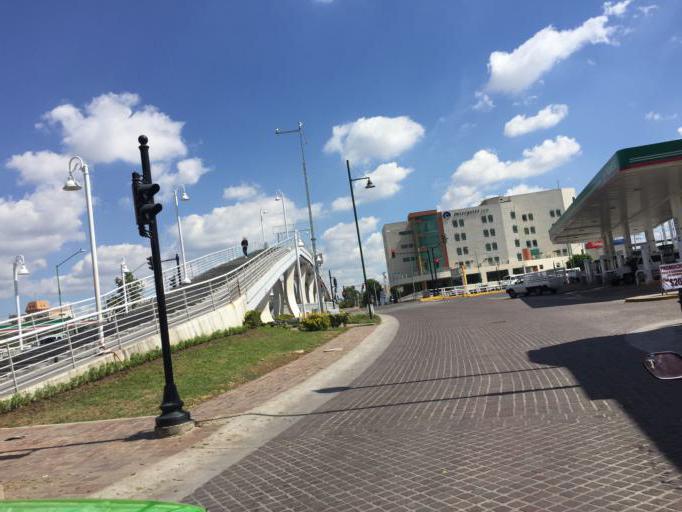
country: MX
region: Guanajuato
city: Leon
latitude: 21.1176
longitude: -101.6682
